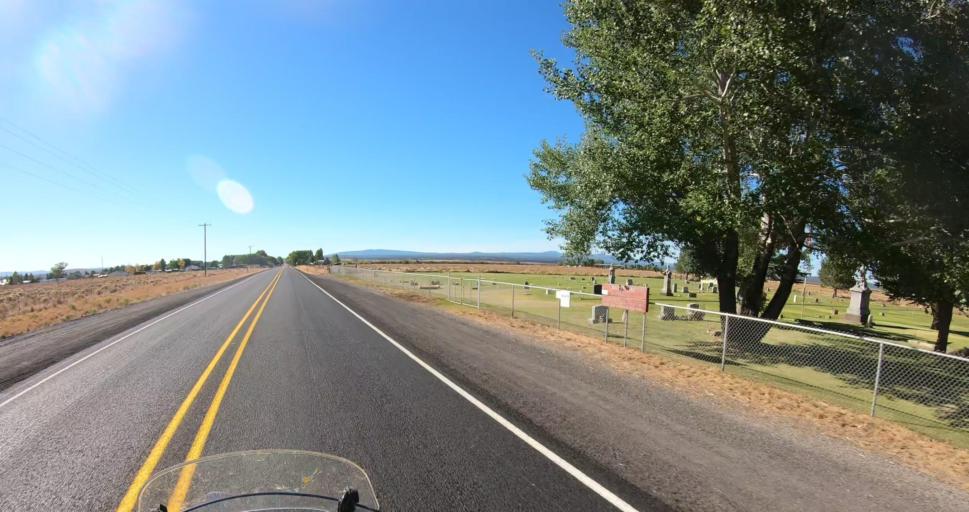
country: US
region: Oregon
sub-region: Deschutes County
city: La Pine
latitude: 43.1276
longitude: -121.0361
